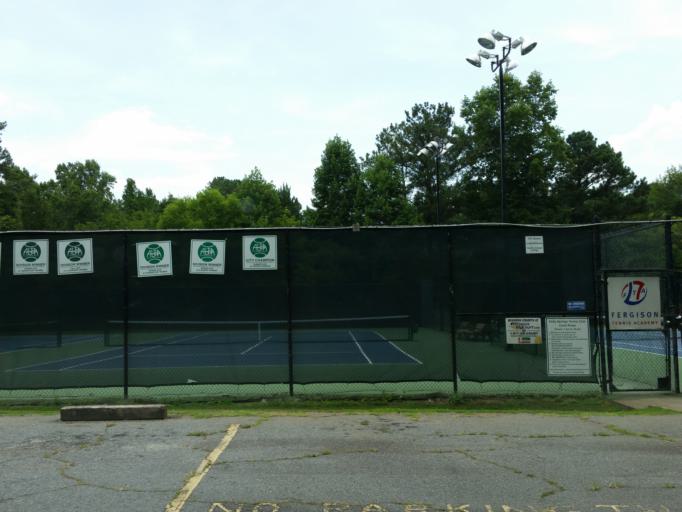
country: US
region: Georgia
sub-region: Cherokee County
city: Woodstock
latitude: 34.0188
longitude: -84.4791
